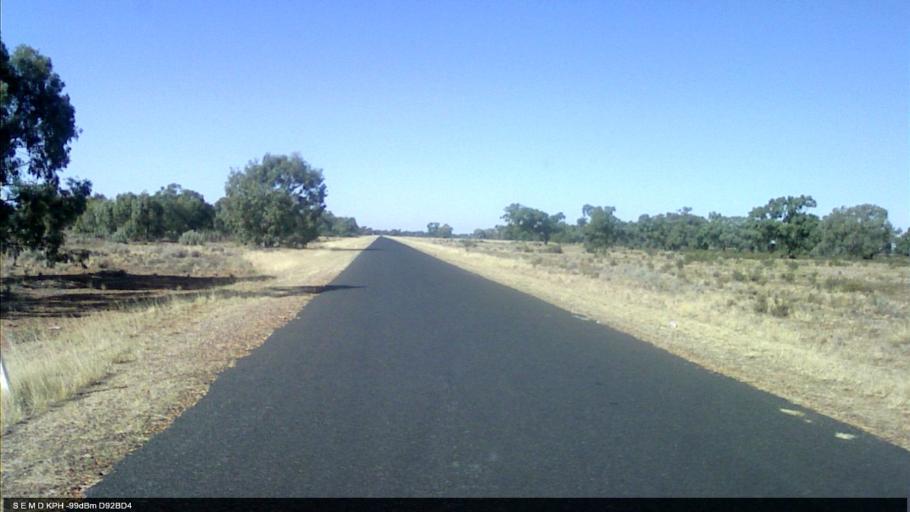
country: AU
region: New South Wales
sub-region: Bogan
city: Nyngan
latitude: -31.7741
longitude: 147.1266
